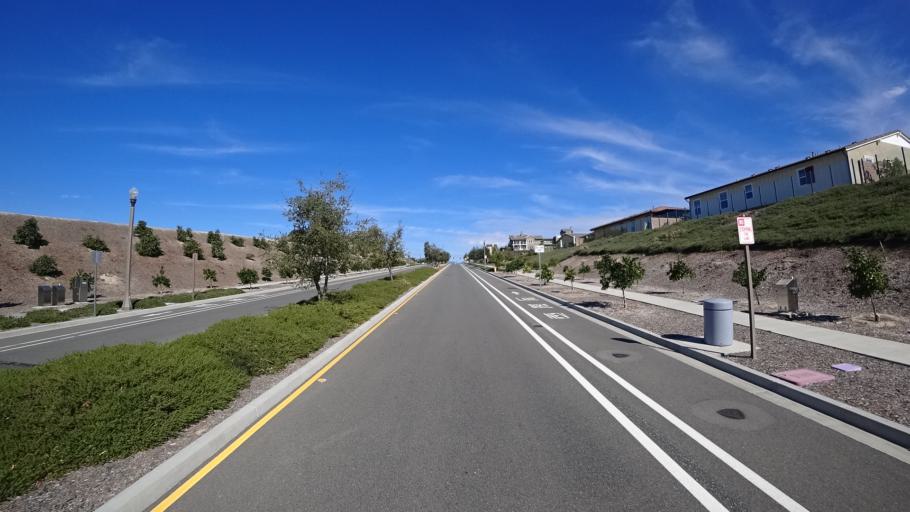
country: US
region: California
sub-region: Orange County
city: Ladera Ranch
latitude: 33.5434
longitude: -117.6025
